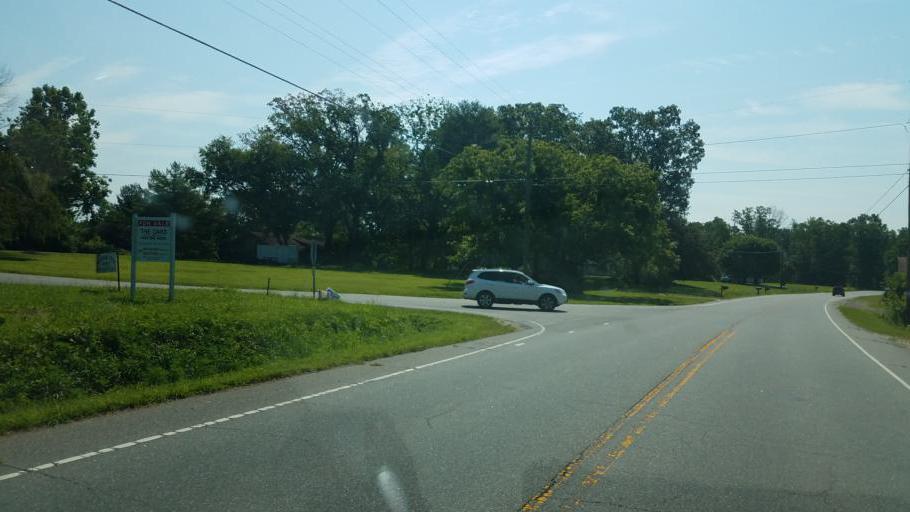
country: US
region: North Carolina
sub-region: Burke County
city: Glen Alpine
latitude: 35.7931
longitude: -81.7626
